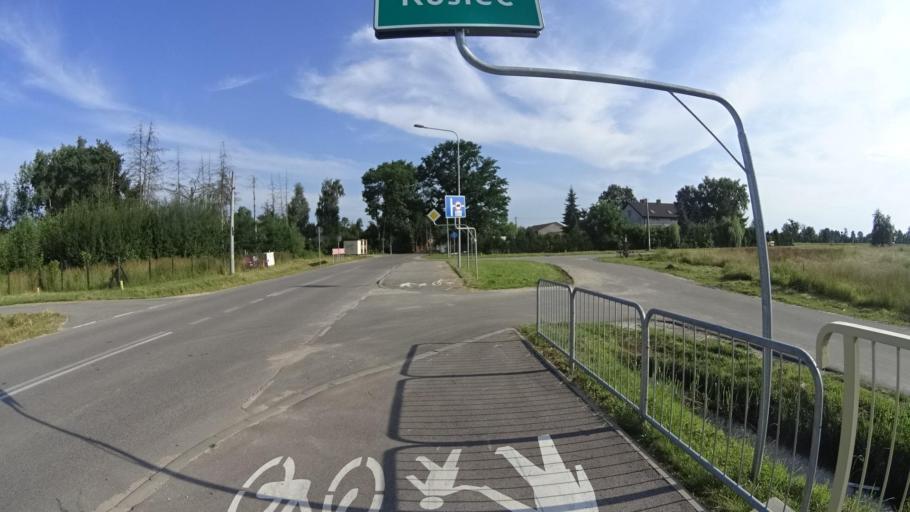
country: PL
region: Masovian Voivodeship
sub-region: Powiat pruszkowski
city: Nadarzyn
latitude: 52.0818
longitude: 20.7946
